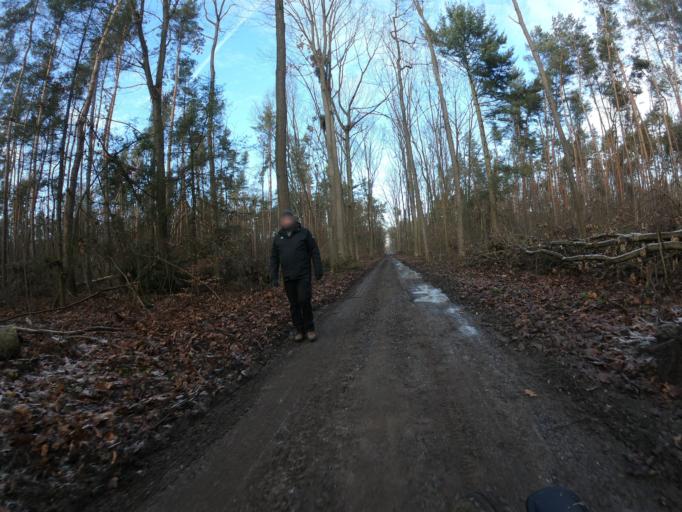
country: DE
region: Hesse
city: Morfelden-Walldorf
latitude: 49.9640
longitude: 8.5933
